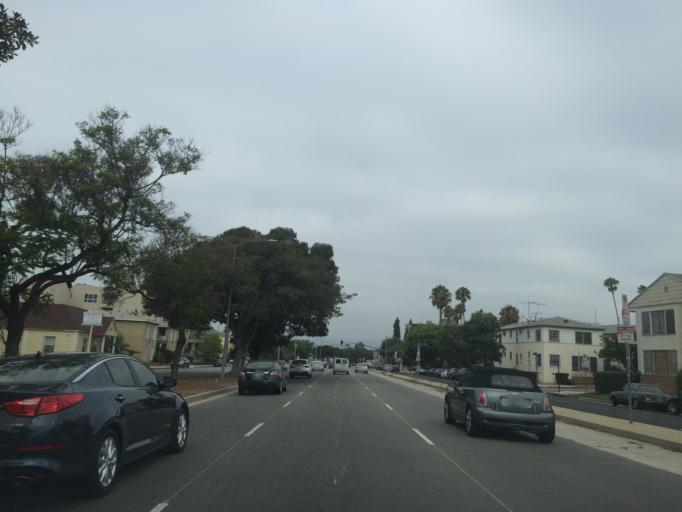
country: US
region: California
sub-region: Los Angeles County
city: West Hollywood
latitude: 34.0547
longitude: -118.3565
